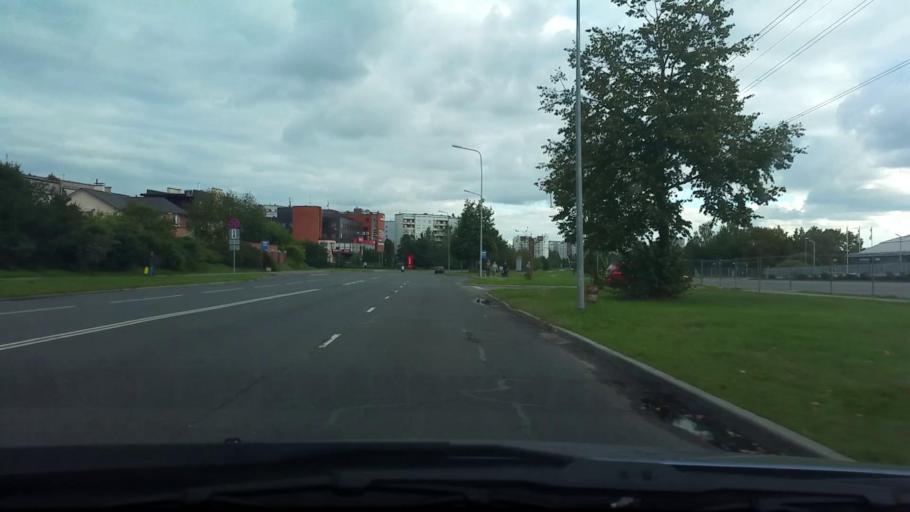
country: LV
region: Stopini
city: Ulbroka
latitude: 56.9709
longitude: 24.2291
